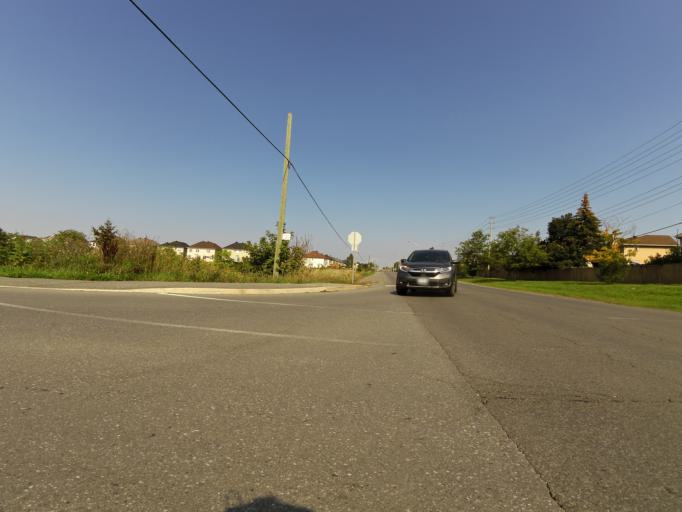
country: CA
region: Ontario
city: Bells Corners
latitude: 45.2710
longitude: -75.7753
